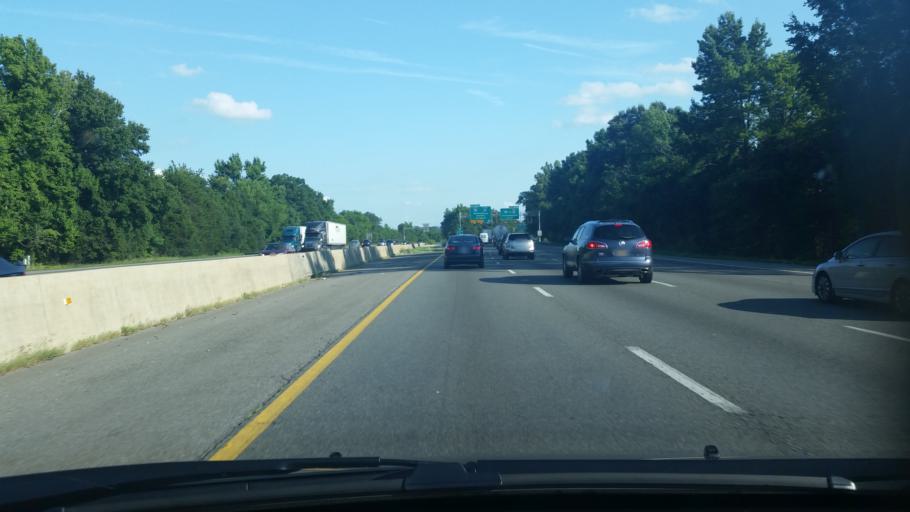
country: US
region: Virginia
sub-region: Henrico County
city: Chamberlayne
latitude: 37.6775
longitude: -77.4499
